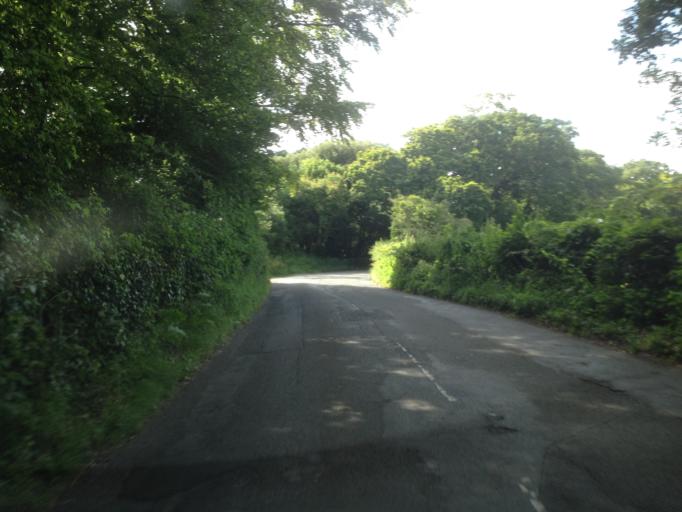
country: GB
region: England
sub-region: Isle of Wight
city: Bembridge
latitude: 50.6806
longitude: -1.0881
